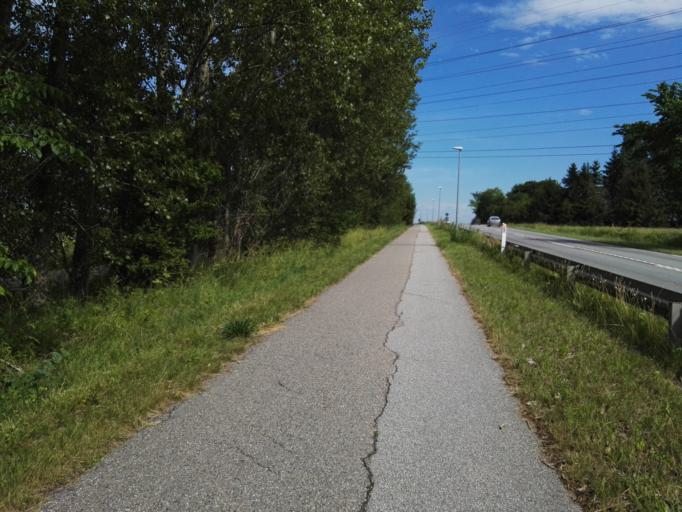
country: DK
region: Capital Region
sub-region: Egedal Kommune
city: Olstykke
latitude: 55.8108
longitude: 12.1652
